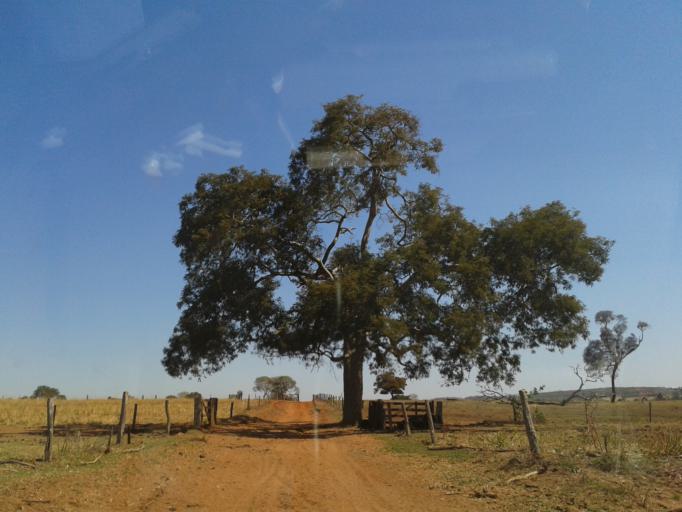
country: BR
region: Minas Gerais
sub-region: Santa Vitoria
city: Santa Vitoria
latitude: -19.0813
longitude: -50.0700
